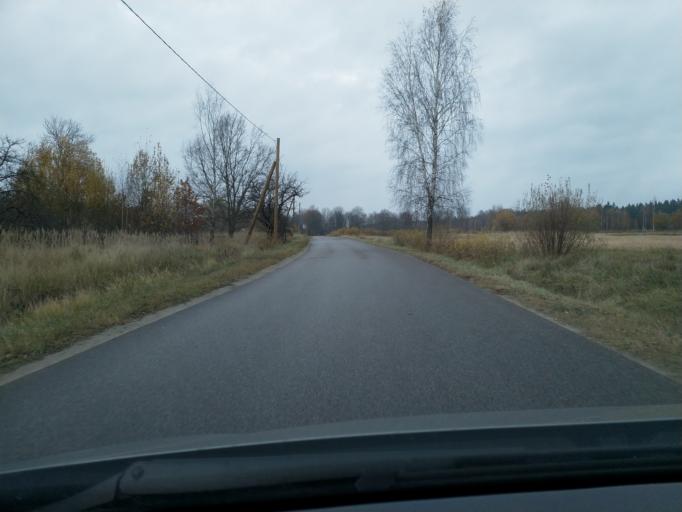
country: LV
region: Kuldigas Rajons
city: Kuldiga
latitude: 56.9778
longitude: 21.9784
